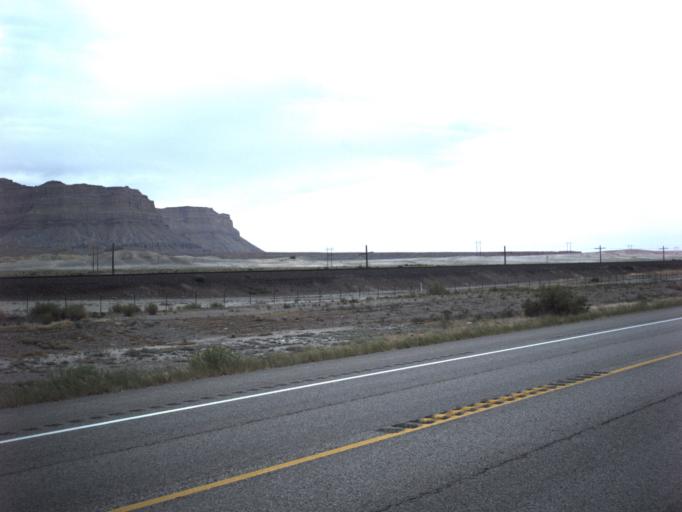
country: US
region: Utah
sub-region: Carbon County
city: East Carbon City
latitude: 39.1052
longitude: -110.3252
